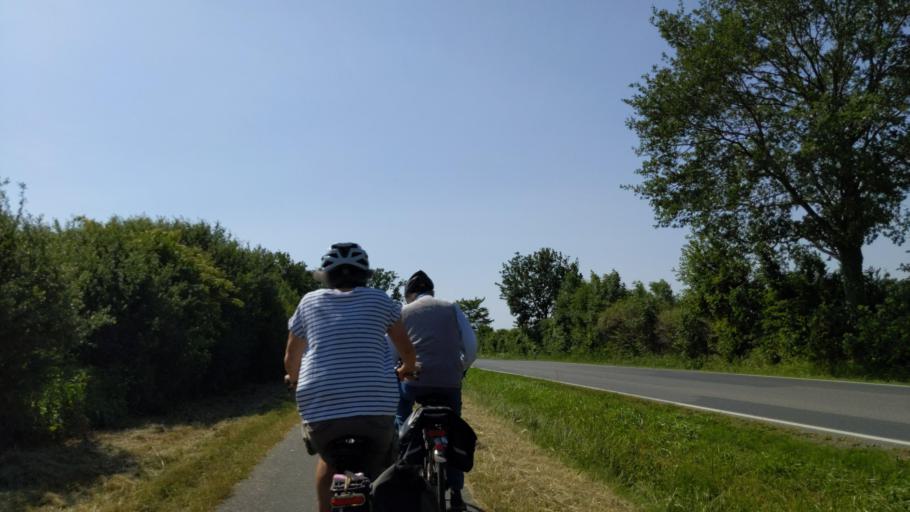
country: DE
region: Schleswig-Holstein
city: Klempau
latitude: 53.7526
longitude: 10.6573
